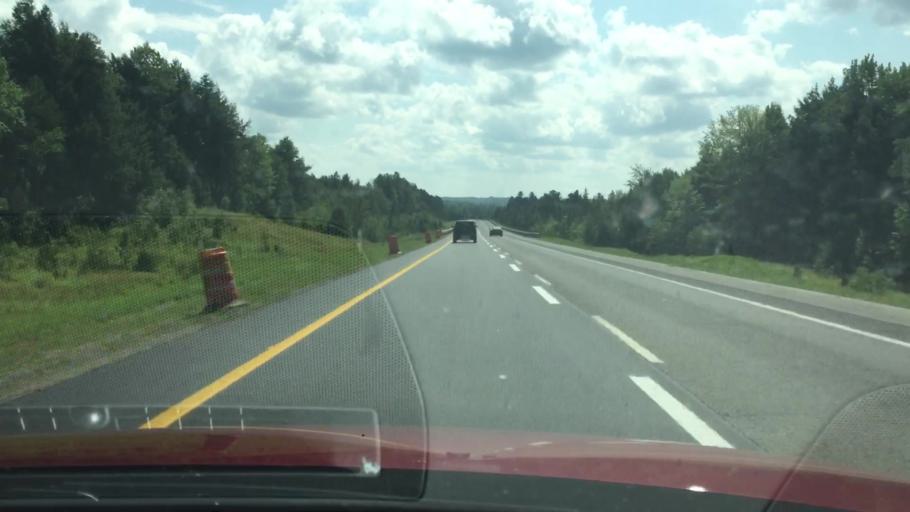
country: US
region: Maine
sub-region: Penobscot County
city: Medway
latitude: 45.6524
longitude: -68.4995
